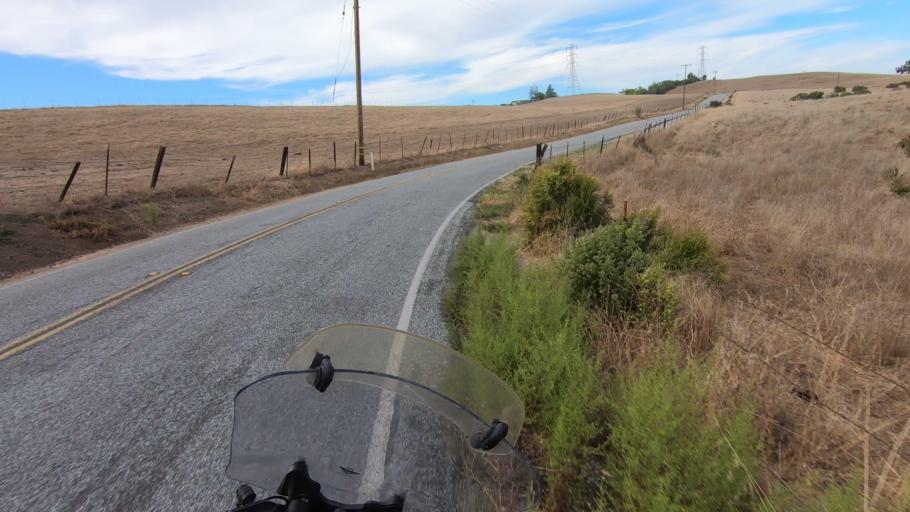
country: US
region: California
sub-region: Santa Clara County
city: East Foothills
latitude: 37.4292
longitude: -121.8004
